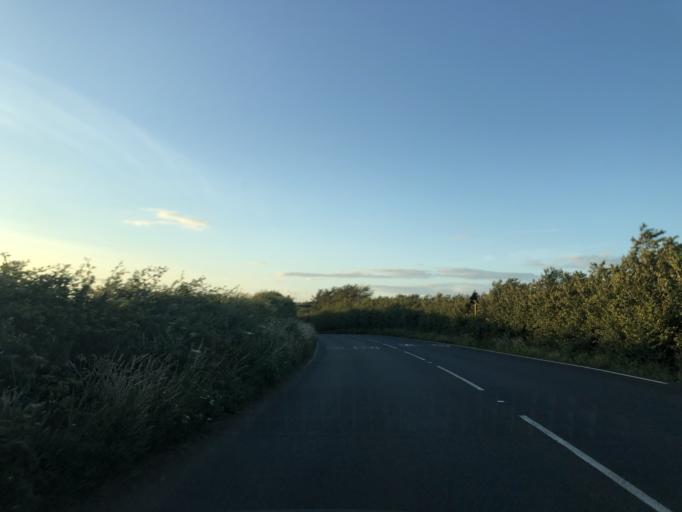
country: GB
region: England
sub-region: Isle of Wight
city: Newport
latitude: 50.6627
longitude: -1.2848
